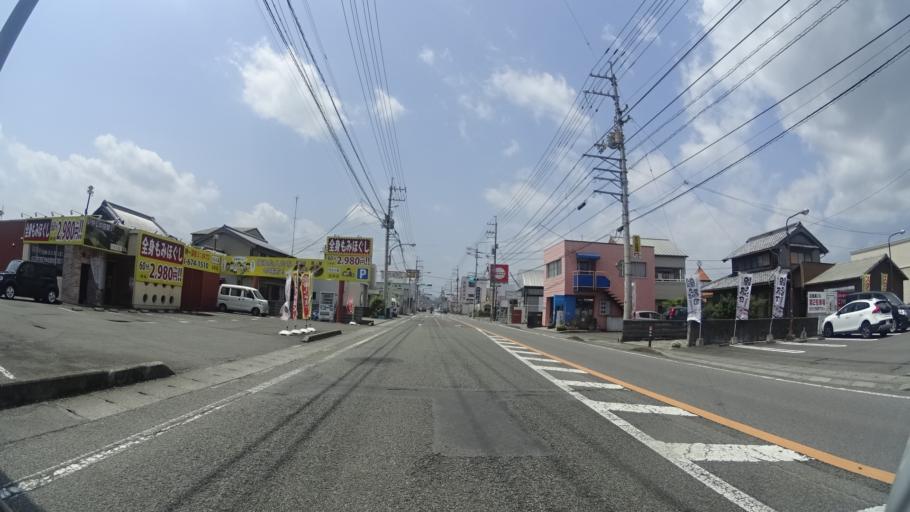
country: JP
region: Tokushima
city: Ishii
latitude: 34.0695
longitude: 134.4523
